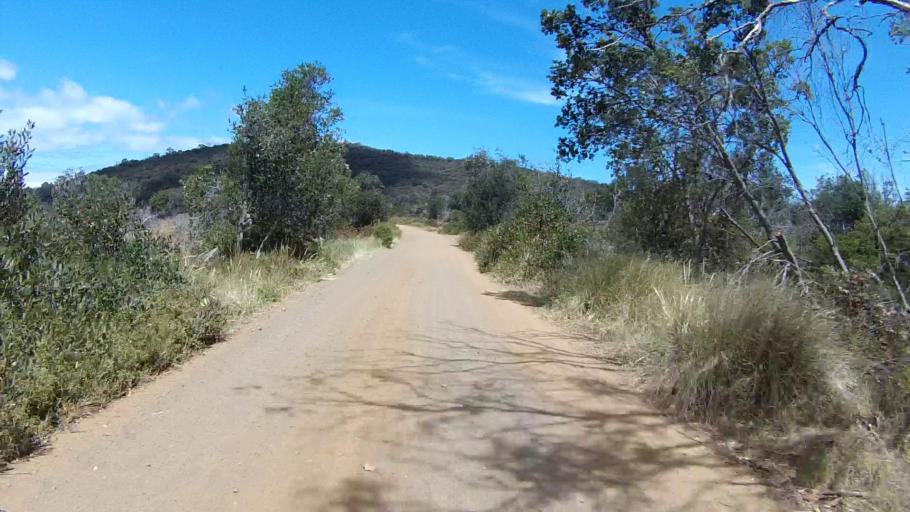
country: AU
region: Tasmania
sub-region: Sorell
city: Sorell
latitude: -42.8744
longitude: 147.6450
